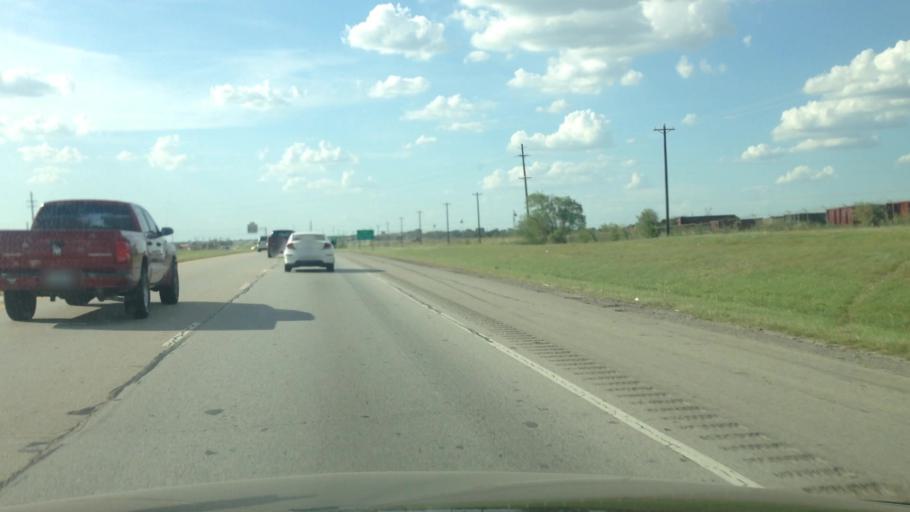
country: US
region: Texas
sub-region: Tarrant County
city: Blue Mound
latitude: 32.9083
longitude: -97.3414
